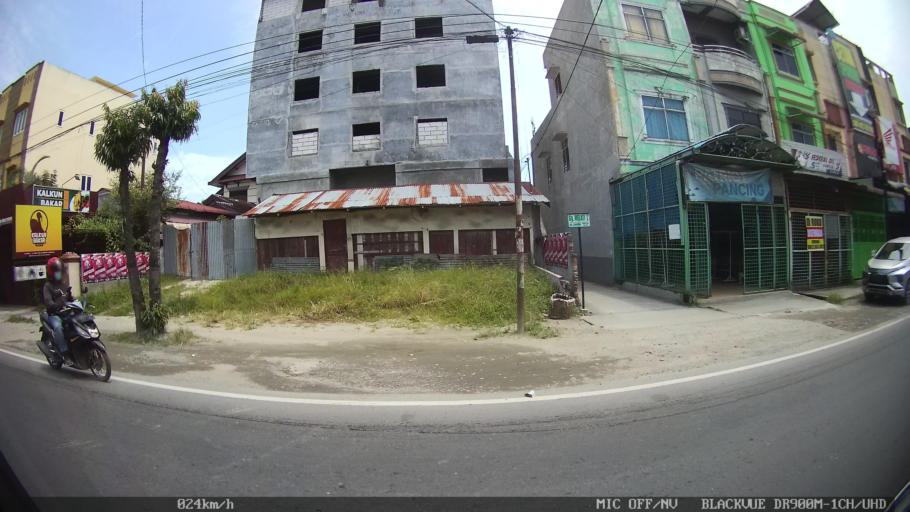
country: ID
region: North Sumatra
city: Sunggal
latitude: 3.5856
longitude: 98.6211
